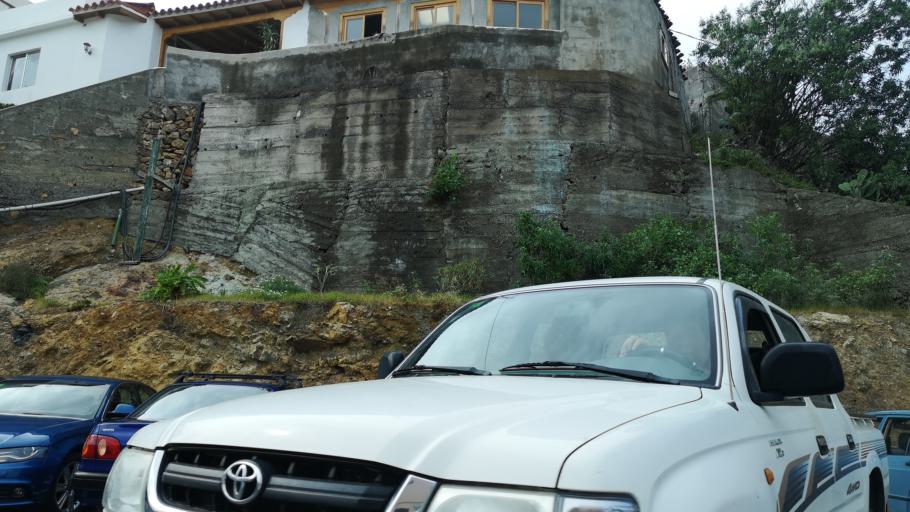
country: ES
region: Canary Islands
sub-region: Provincia de Santa Cruz de Tenerife
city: Vallehermosa
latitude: 28.1810
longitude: -17.2664
